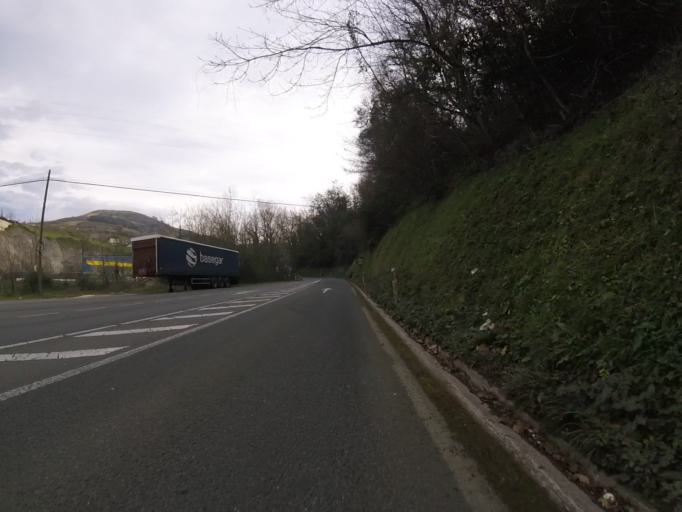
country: ES
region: Basque Country
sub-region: Provincia de Guipuzcoa
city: Aizarnazabal
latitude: 43.2534
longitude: -2.2431
